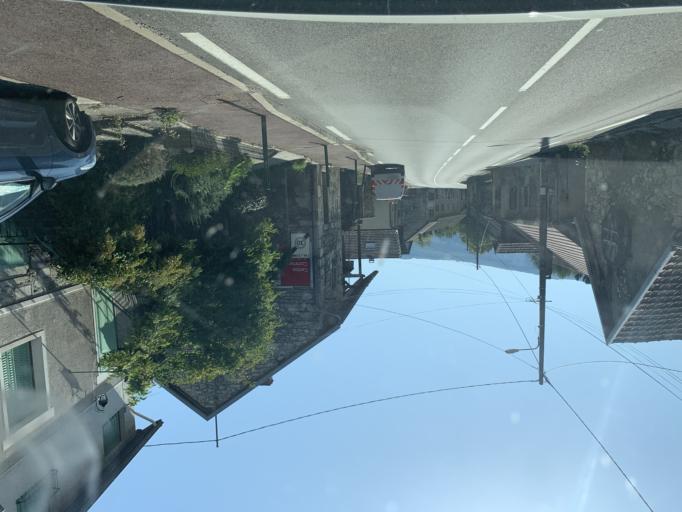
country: FR
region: Rhone-Alpes
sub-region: Departement de la Savoie
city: Yenne
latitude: 45.6749
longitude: 5.6783
